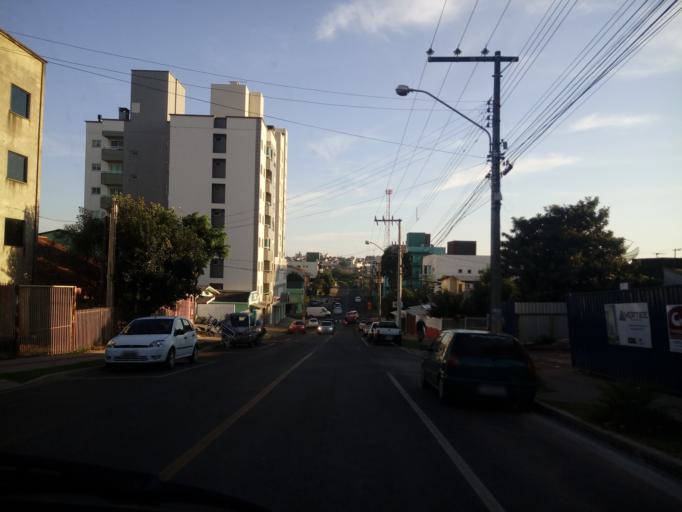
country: BR
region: Santa Catarina
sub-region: Chapeco
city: Chapeco
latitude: -27.0913
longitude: -52.6114
